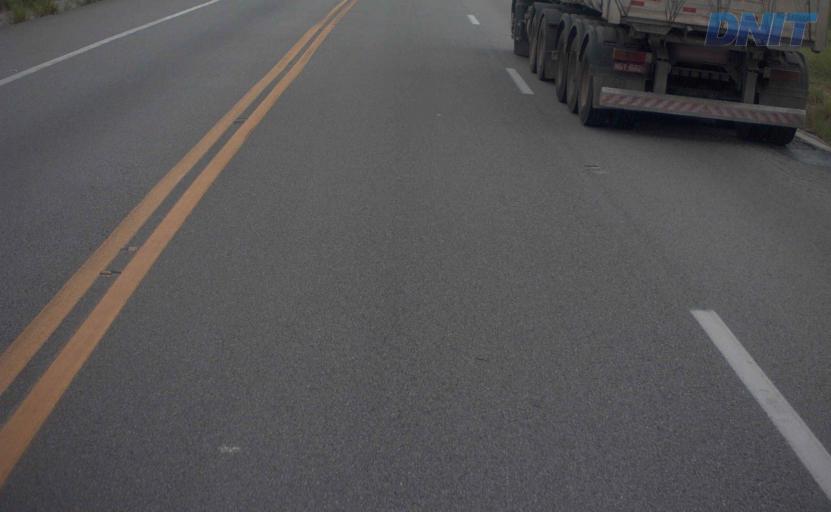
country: BR
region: Minas Gerais
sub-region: Nova Era
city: Nova Era
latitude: -19.6704
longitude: -42.9705
